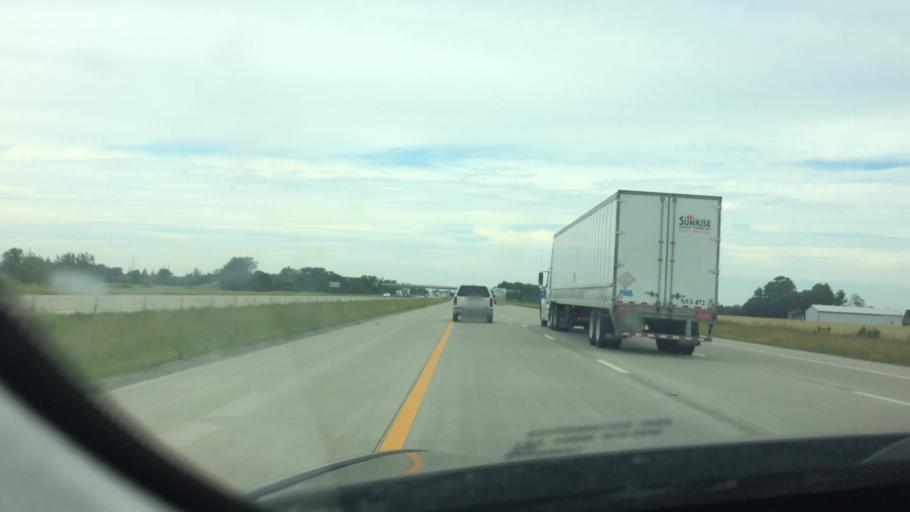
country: US
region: Ohio
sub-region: Wood County
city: Perrysburg
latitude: 41.5026
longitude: -83.6219
